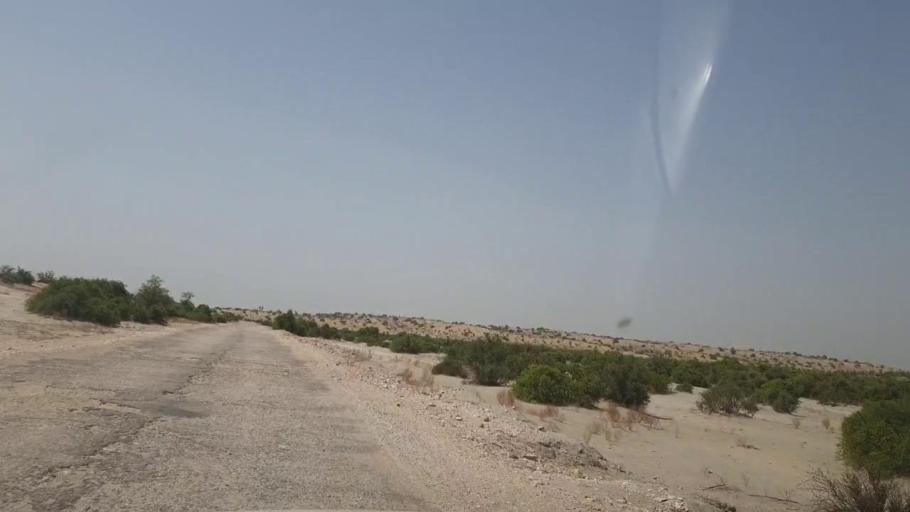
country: PK
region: Sindh
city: Khanpur
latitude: 27.3561
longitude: 69.3180
